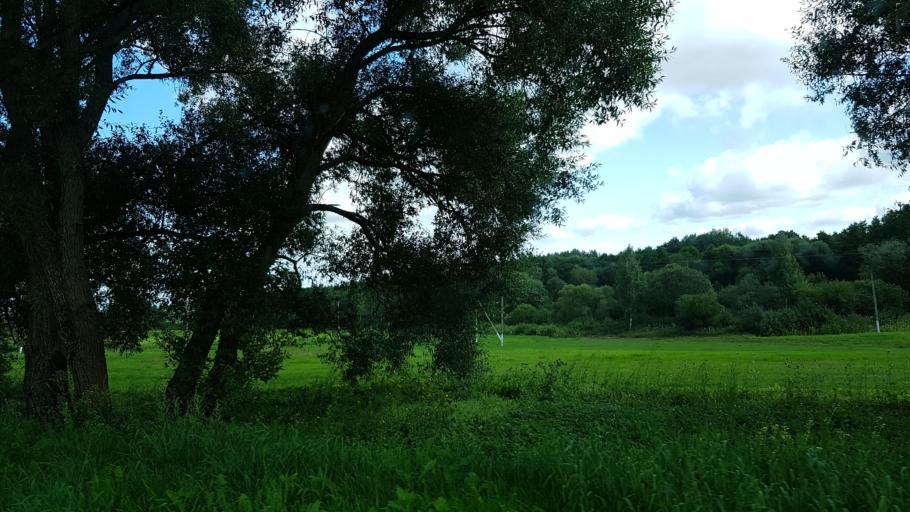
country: BY
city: Fanipol
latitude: 53.7690
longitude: 27.3240
